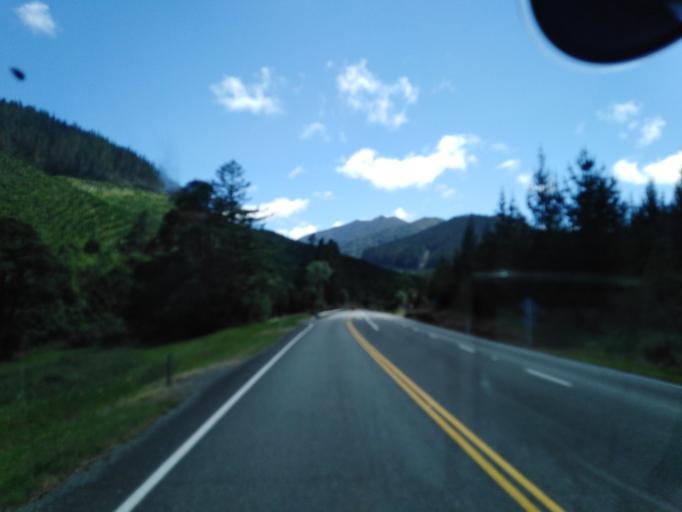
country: NZ
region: Nelson
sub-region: Nelson City
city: Nelson
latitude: -41.1794
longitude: 173.5594
